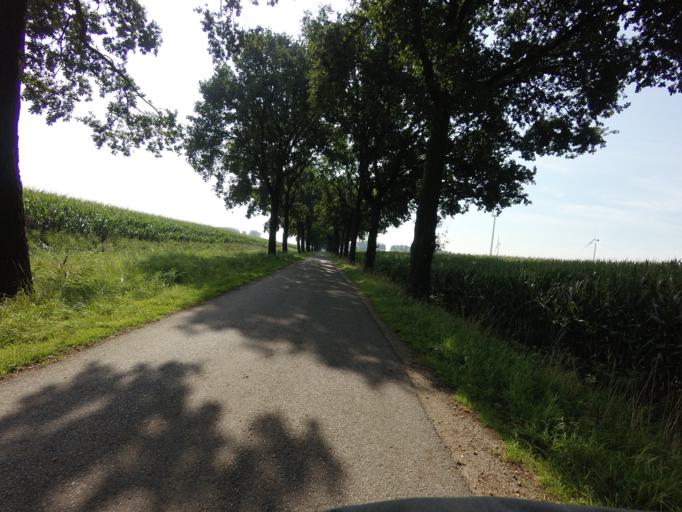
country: NL
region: Gelderland
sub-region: Gemeente Rheden
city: Rheden
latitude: 51.9831
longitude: 6.0216
